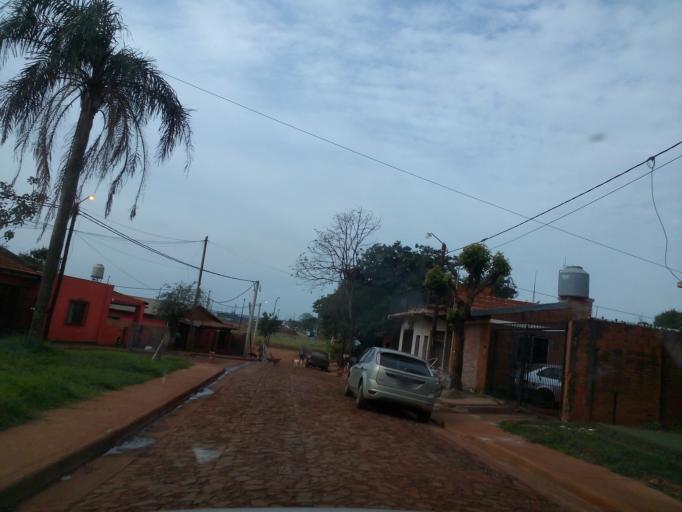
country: AR
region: Misiones
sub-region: Departamento de Capital
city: Posadas
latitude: -27.4224
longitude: -55.8926
